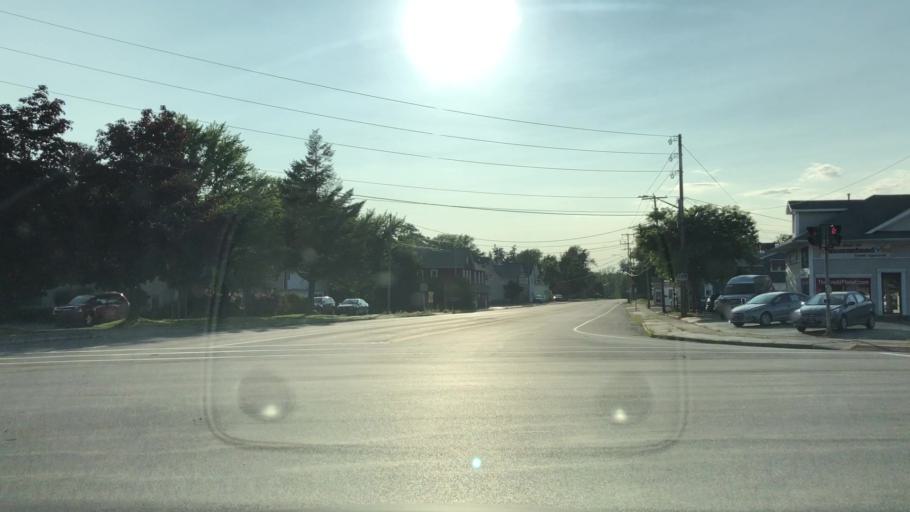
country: US
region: New York
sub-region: Erie County
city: West Seneca
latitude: 42.8552
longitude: -78.7547
